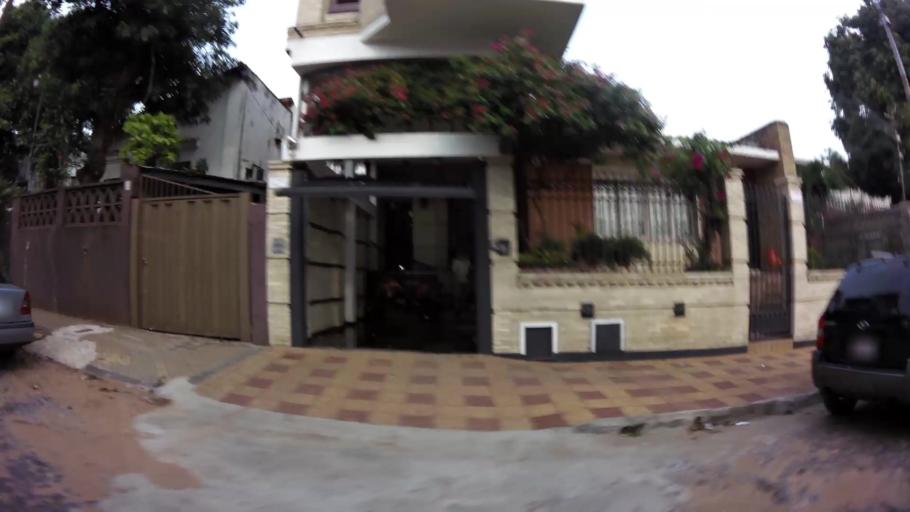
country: PY
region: Asuncion
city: Asuncion
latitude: -25.3070
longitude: -57.6134
